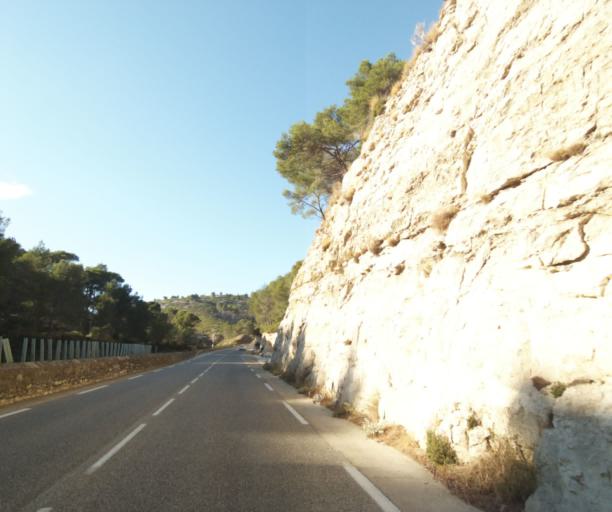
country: FR
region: Provence-Alpes-Cote d'Azur
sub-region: Departement des Bouches-du-Rhone
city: La Ciotat
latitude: 43.2068
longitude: 5.5841
